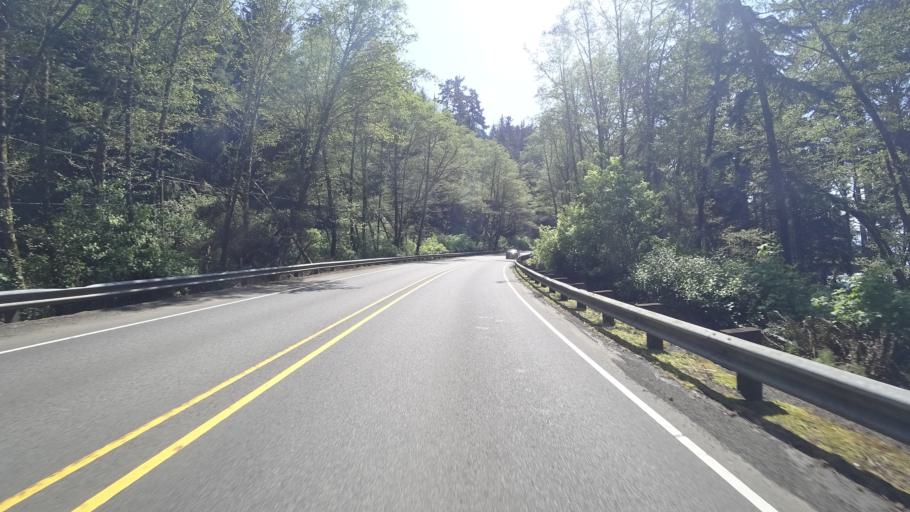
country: US
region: Oregon
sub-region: Lincoln County
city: Depoe Bay
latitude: 44.7881
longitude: -124.0659
